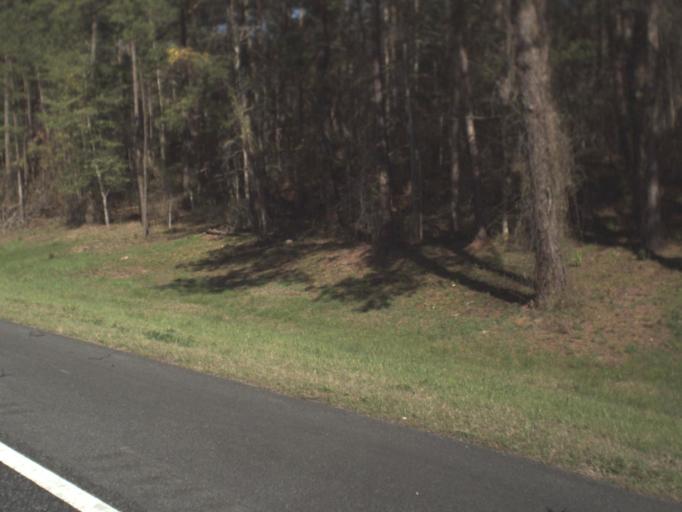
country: US
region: Florida
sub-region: Leon County
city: Tallahassee
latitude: 30.4993
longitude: -84.2144
